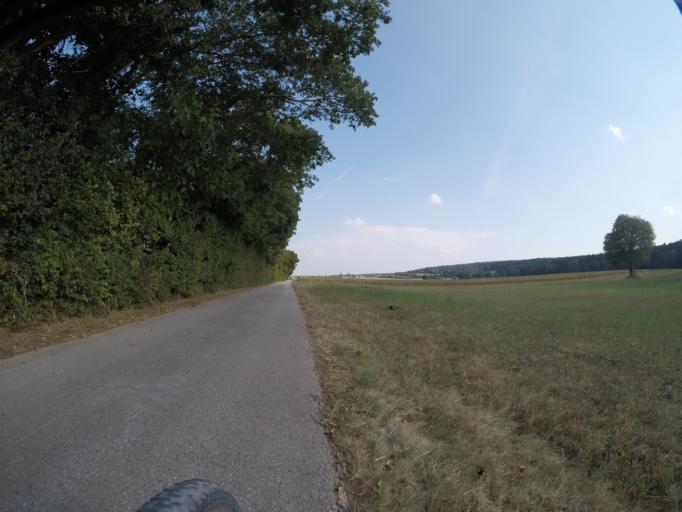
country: AT
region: Lower Austria
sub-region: Politischer Bezirk Baden
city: Hirtenberg
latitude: 47.9649
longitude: 16.1508
